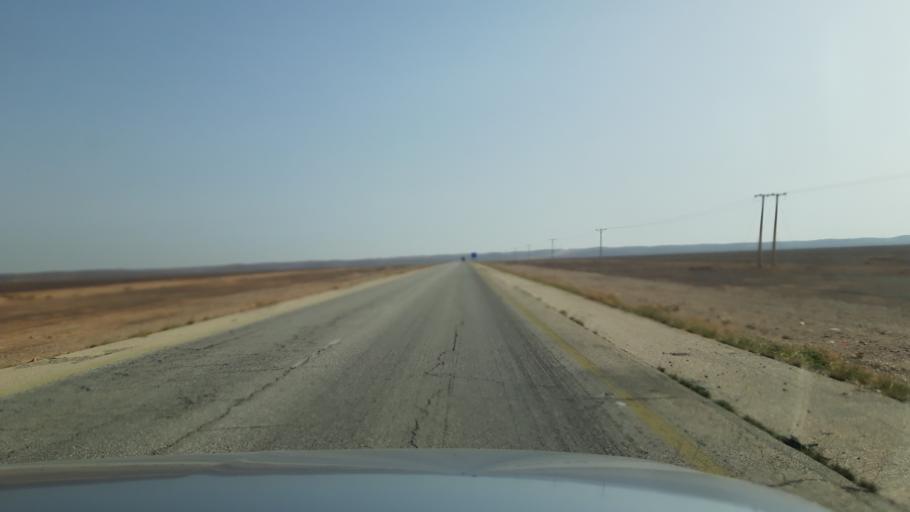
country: JO
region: Amman
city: Al Azraq ash Shamali
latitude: 31.8362
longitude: 36.6344
